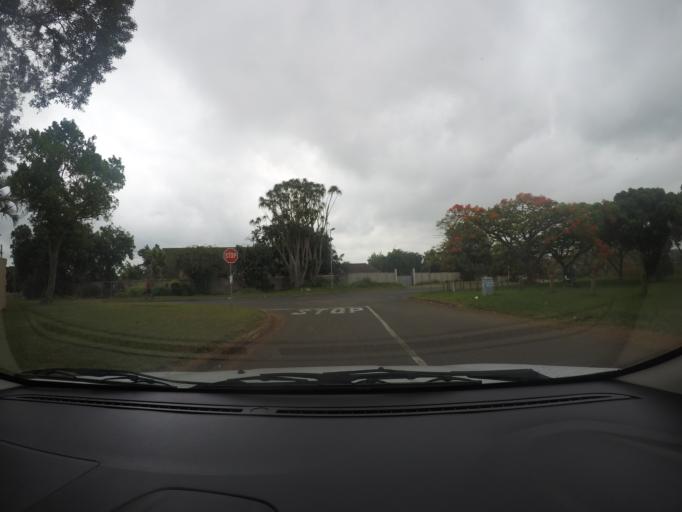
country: ZA
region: KwaZulu-Natal
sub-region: uThungulu District Municipality
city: Empangeni
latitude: -28.7632
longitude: 31.8920
